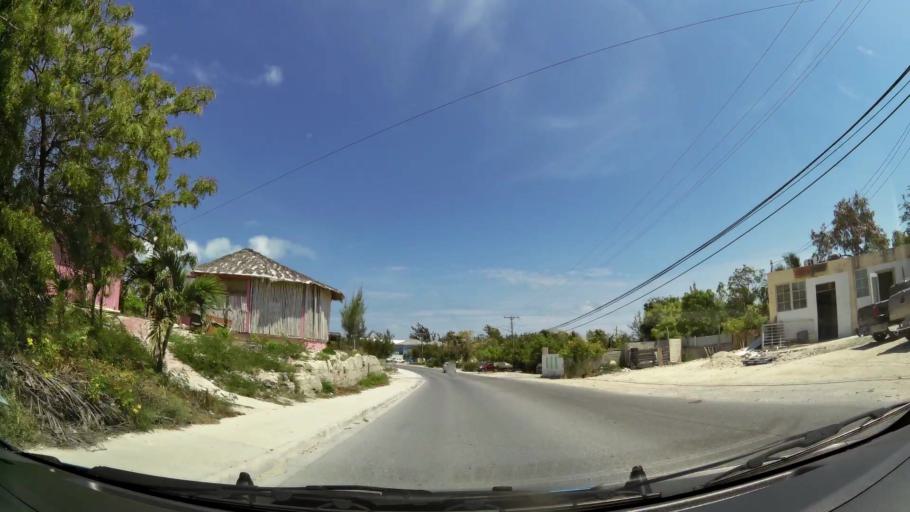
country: BS
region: Mayaguana
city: Abraham's Bay
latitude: 21.7679
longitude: -72.2581
